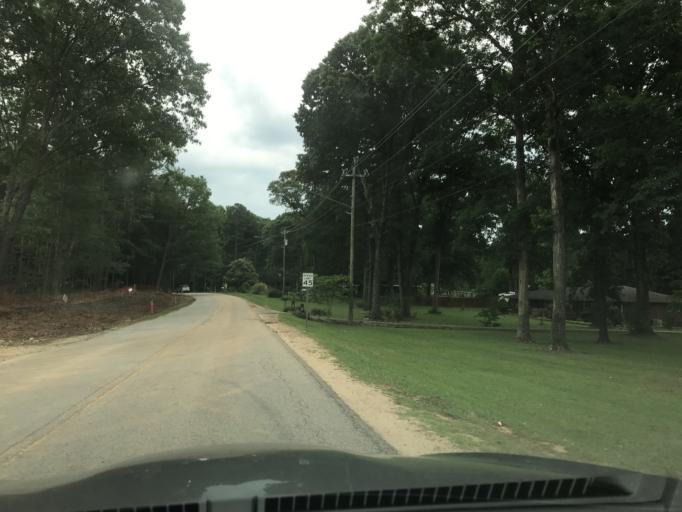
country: US
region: North Carolina
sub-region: Wake County
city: Raleigh
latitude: 35.8614
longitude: -78.5879
